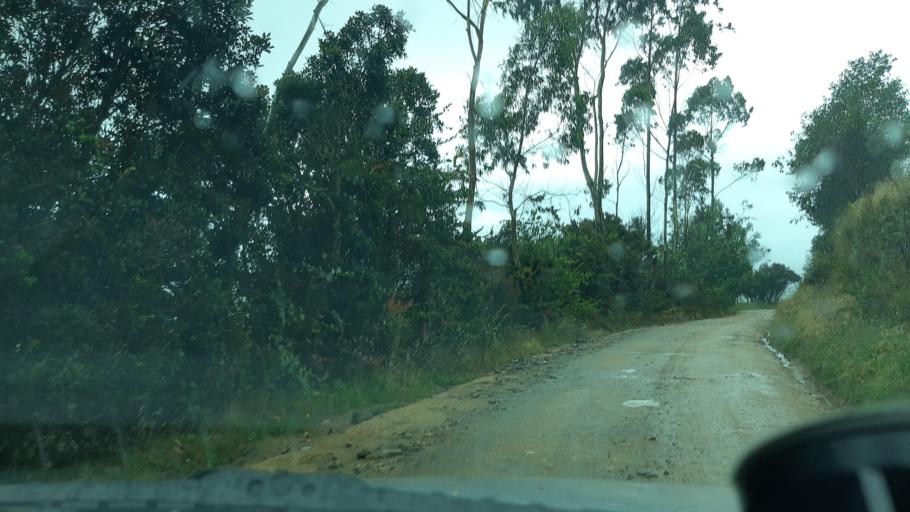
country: CO
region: Cundinamarca
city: Villapinzon
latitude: 5.2085
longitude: -73.5652
